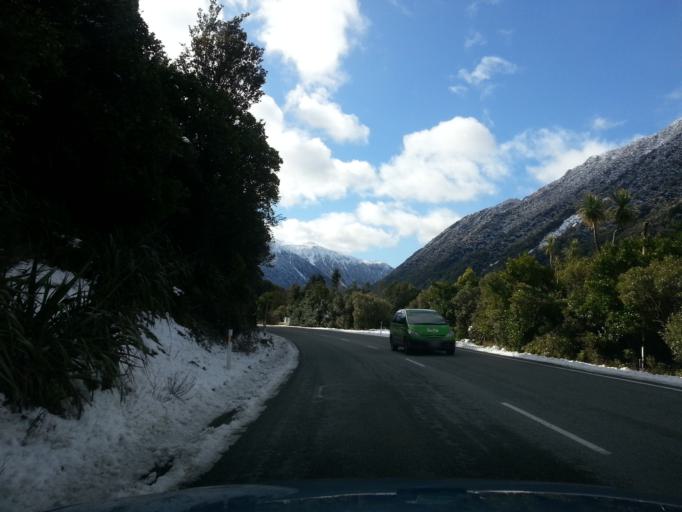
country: NZ
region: West Coast
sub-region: Grey District
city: Greymouth
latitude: -42.8421
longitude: 171.5603
